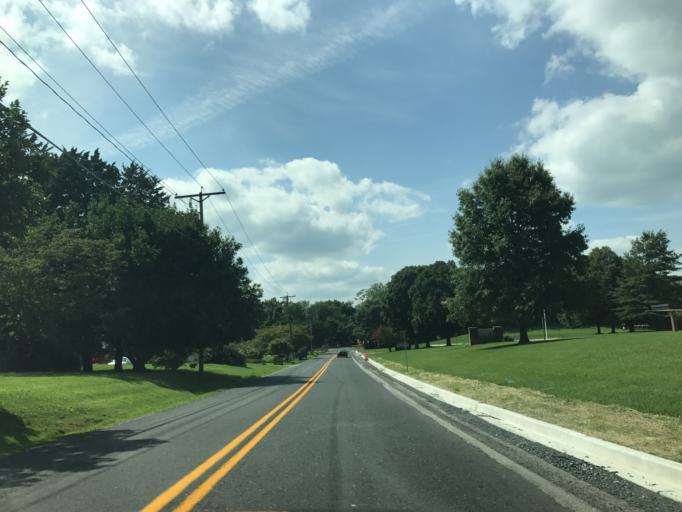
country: US
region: Maryland
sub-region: Harford County
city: South Bel Air
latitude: 39.5554
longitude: -76.2920
